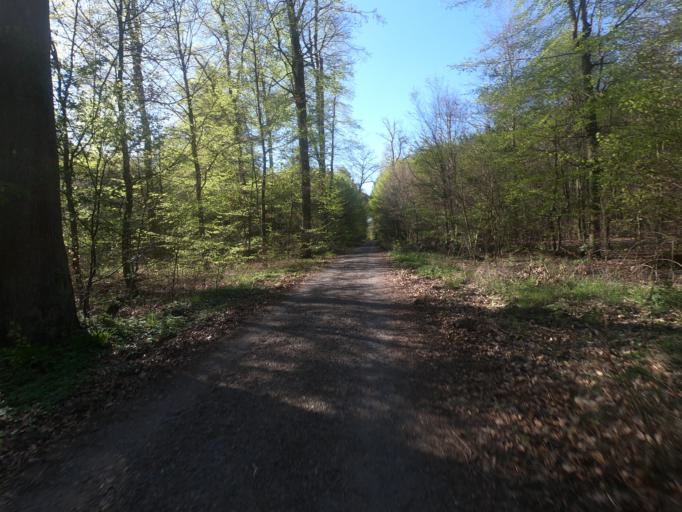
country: DE
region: Hesse
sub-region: Regierungsbezirk Darmstadt
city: Egelsbach
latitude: 49.9763
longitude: 8.7063
